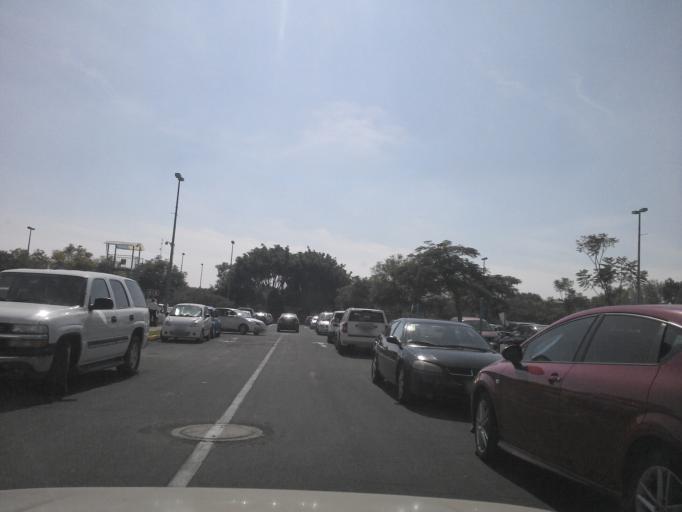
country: MX
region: Jalisco
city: Zapopan2
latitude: 20.7252
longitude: -103.4318
